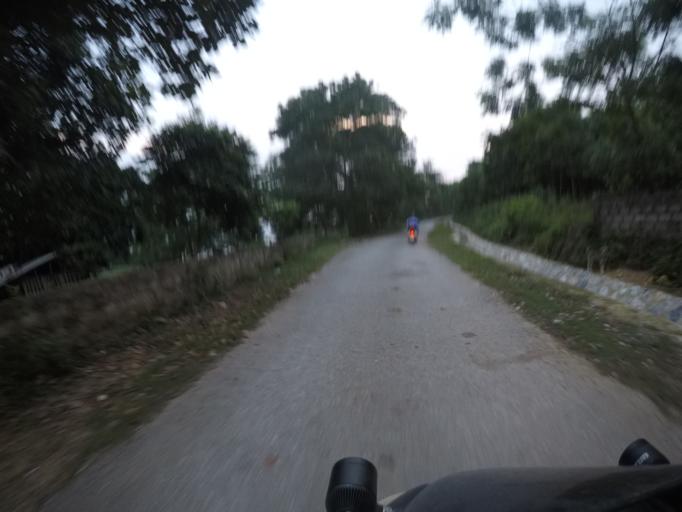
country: VN
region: Thai Nguyen
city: Chua Hang
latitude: 21.5841
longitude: 105.7017
